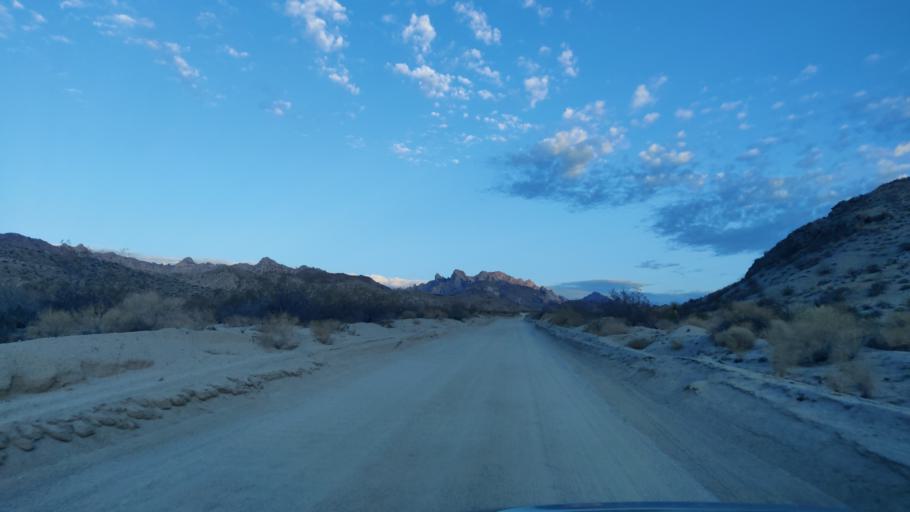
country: US
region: Nevada
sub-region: Clark County
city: Laughlin
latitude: 35.2034
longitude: -114.6698
